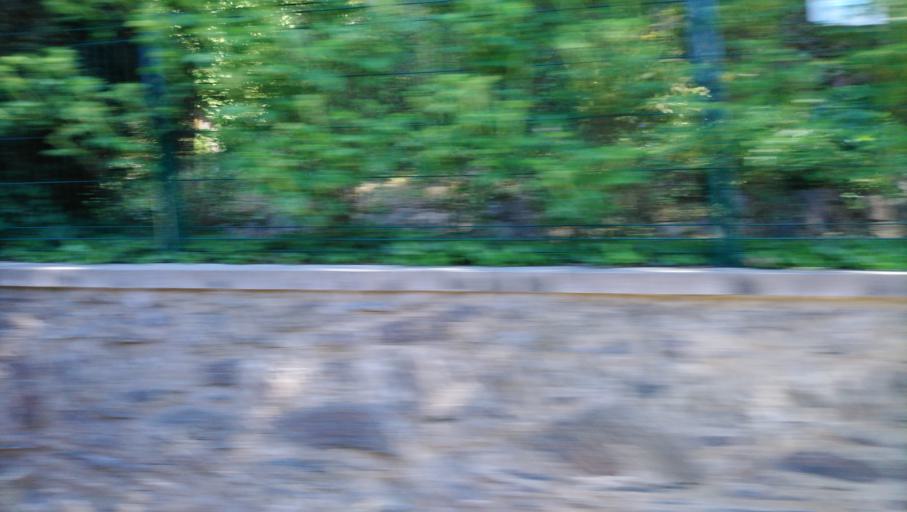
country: LU
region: Diekirch
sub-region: Canton de Vianden
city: Vianden
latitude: 49.9335
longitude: 6.2131
